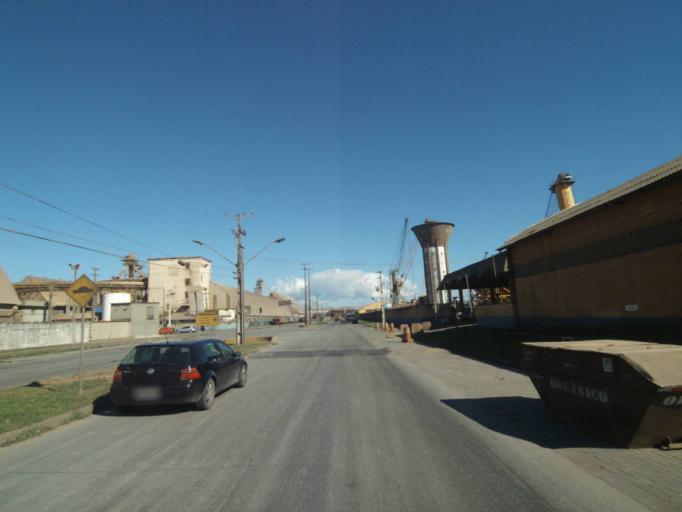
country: BR
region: Parana
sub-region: Paranagua
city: Paranagua
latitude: -25.5033
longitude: -48.5089
